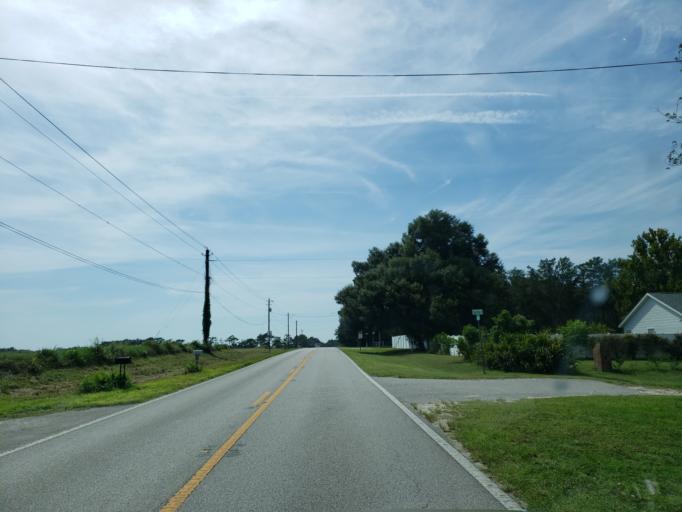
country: US
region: Florida
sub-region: Pasco County
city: San Antonio
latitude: 28.3907
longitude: -82.2992
